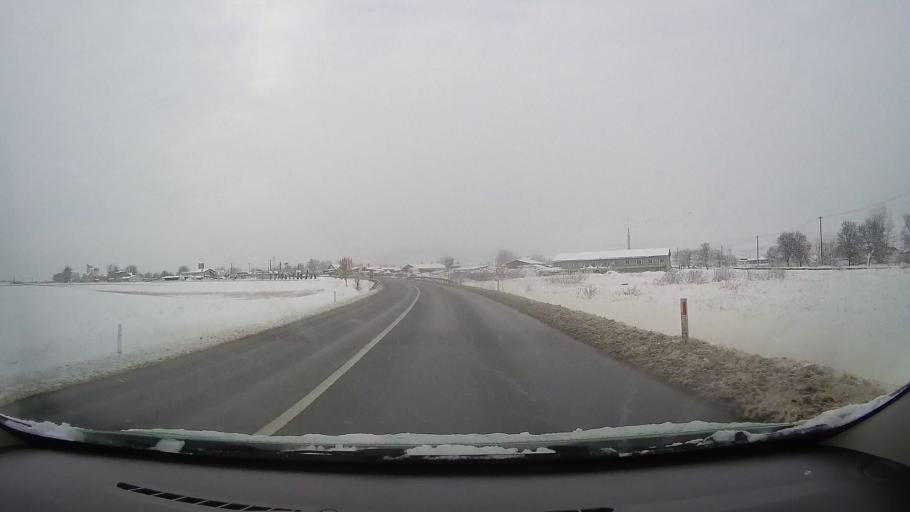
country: RO
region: Alba
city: Vurpar
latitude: 45.9881
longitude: 23.5068
